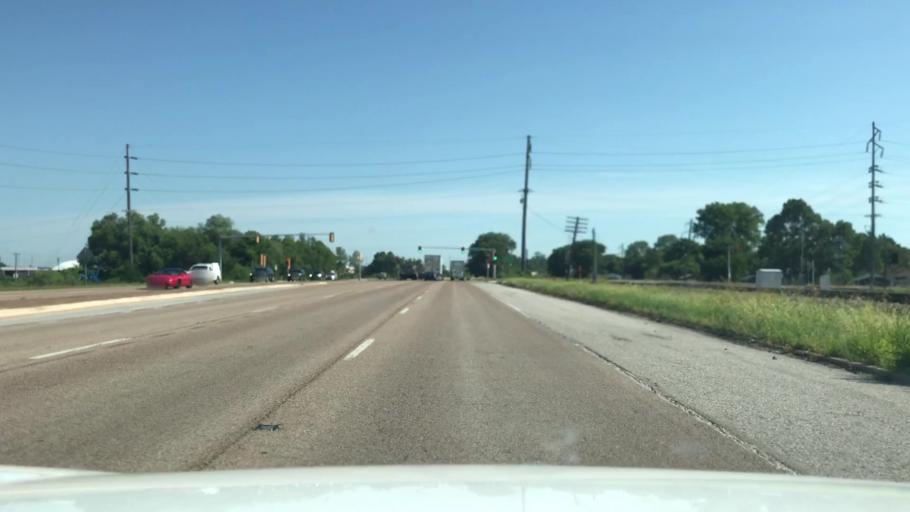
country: US
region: Illinois
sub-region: Madison County
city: Venice
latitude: 38.6790
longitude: -90.1736
